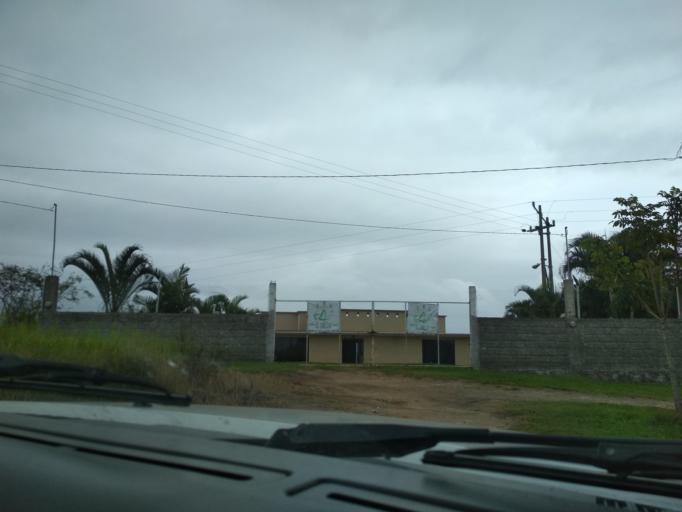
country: MX
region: Veracruz
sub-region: Emiliano Zapata
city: Dos Rios
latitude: 19.5212
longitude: -96.7946
